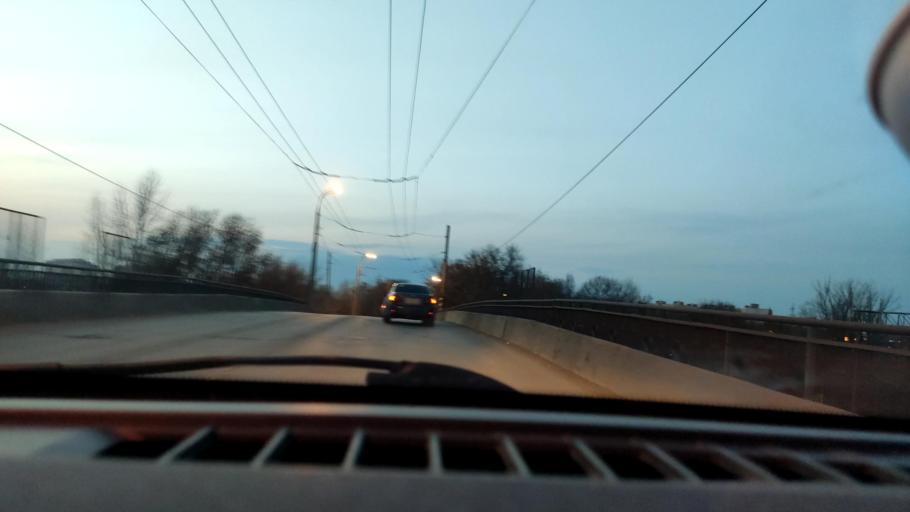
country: RU
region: Samara
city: Samara
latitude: 53.1507
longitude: 50.0934
